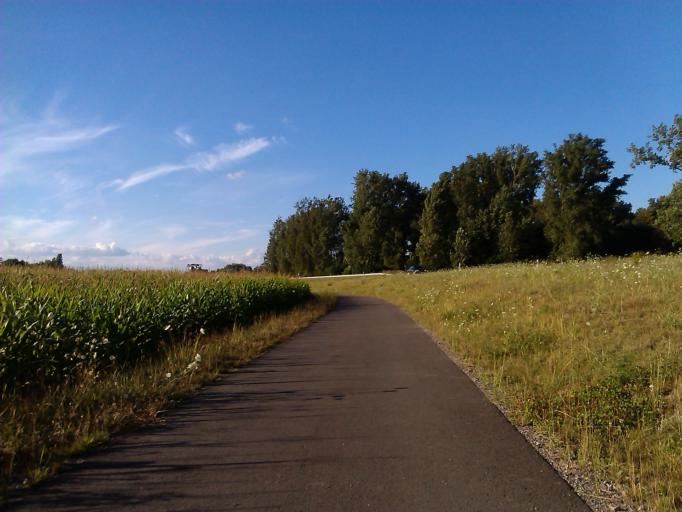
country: DE
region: Rheinland-Pfalz
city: Otterstadt
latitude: 49.3498
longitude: 8.4627
